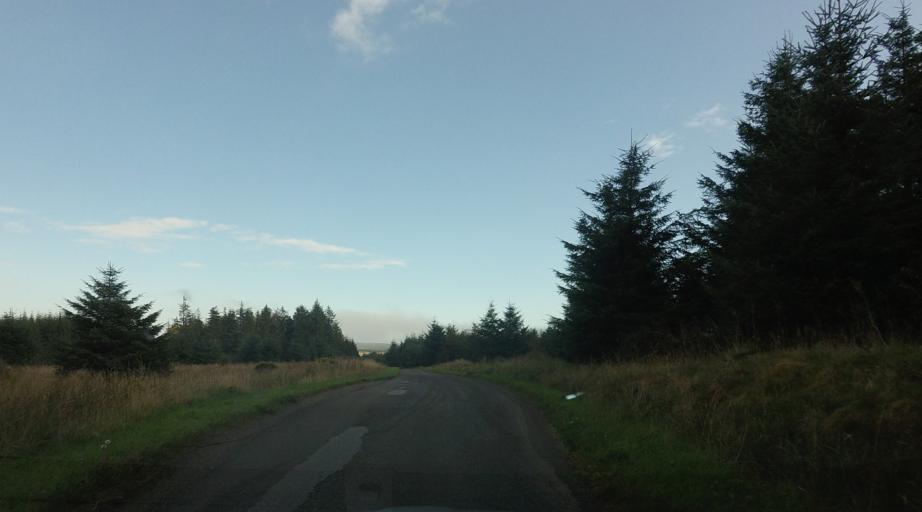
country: GB
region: Scotland
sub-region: Highland
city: Wick
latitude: 58.3348
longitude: -3.3516
